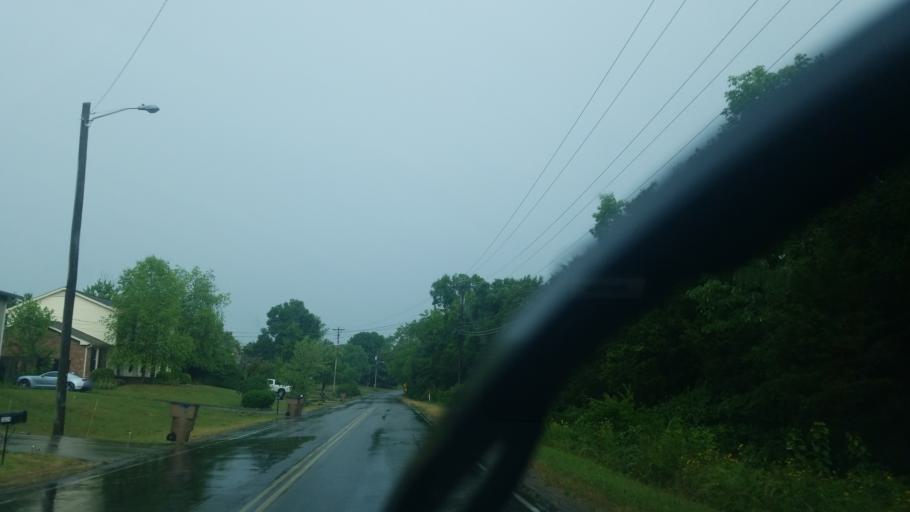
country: US
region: Tennessee
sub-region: Rutherford County
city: La Vergne
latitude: 36.0999
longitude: -86.6034
